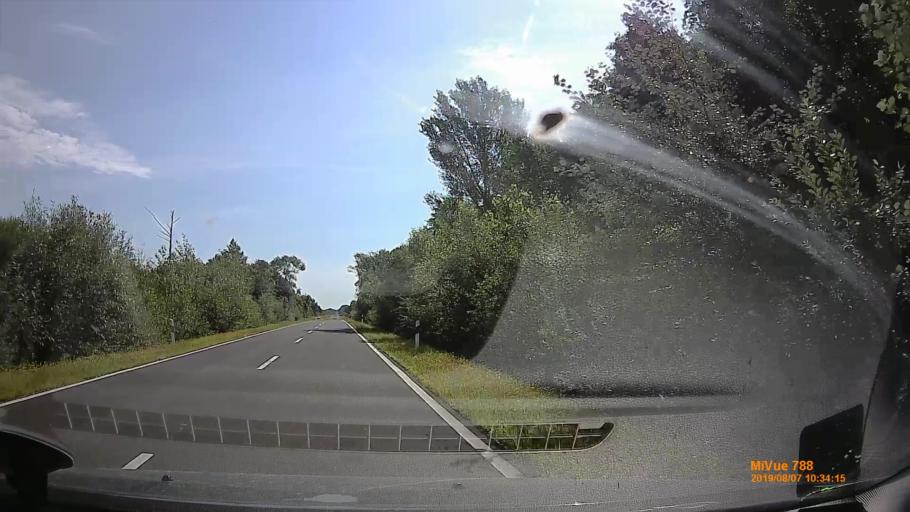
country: SI
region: Lendava-Lendva
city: Lendava
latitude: 46.6170
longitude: 16.4237
